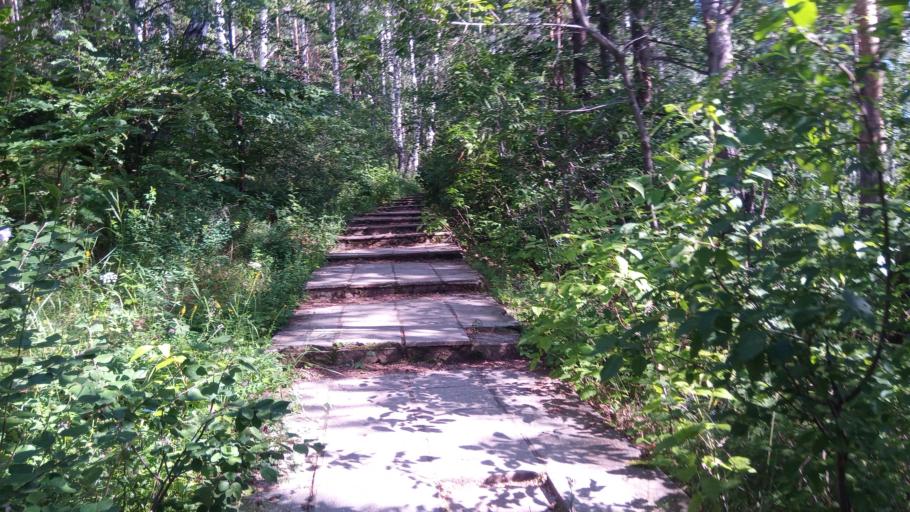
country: RU
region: Chelyabinsk
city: Chebarkul'
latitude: 55.0191
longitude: 60.3102
